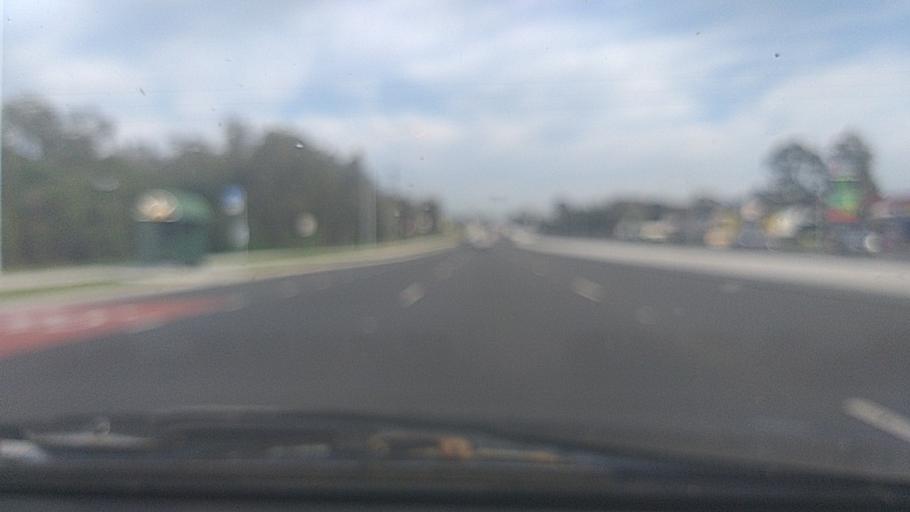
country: AU
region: New South Wales
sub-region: Camden
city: Narellan Vale
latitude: -34.0478
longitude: 150.7612
